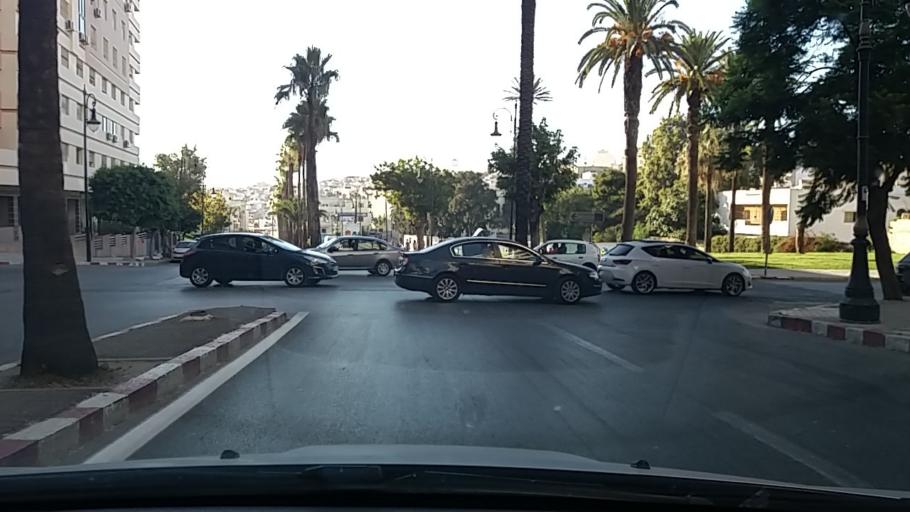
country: MA
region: Tanger-Tetouan
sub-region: Tanger-Assilah
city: Tangier
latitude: 35.7833
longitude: -5.8217
